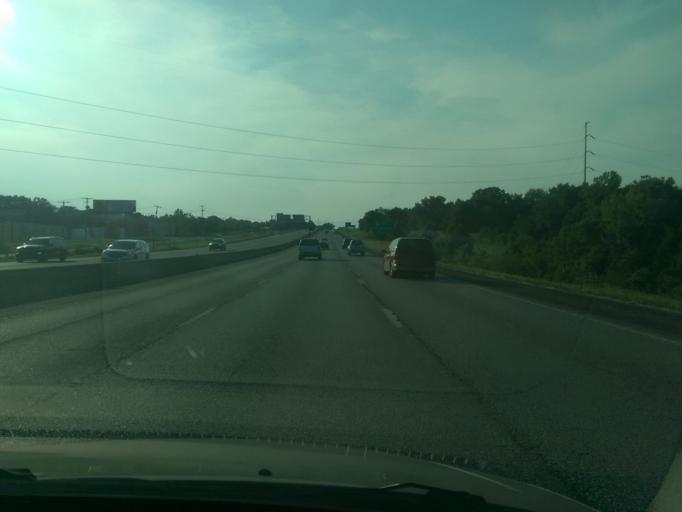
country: US
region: Missouri
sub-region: Platte County
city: Riverside
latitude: 39.2013
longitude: -94.6279
